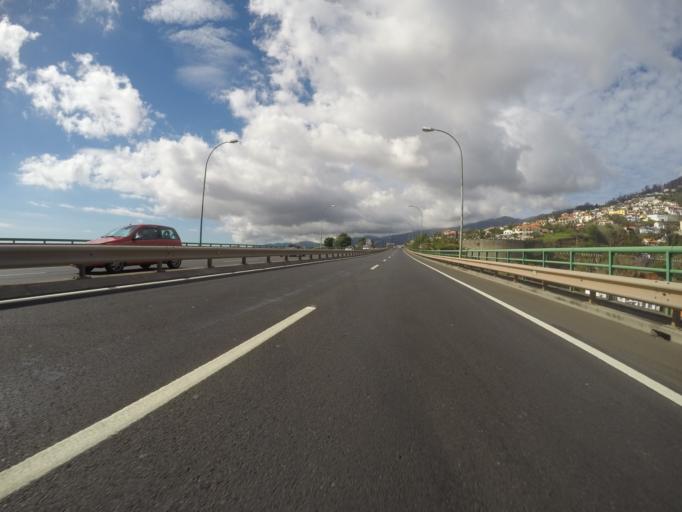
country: PT
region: Madeira
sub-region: Funchal
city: Nossa Senhora do Monte
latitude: 32.6565
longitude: -16.8847
